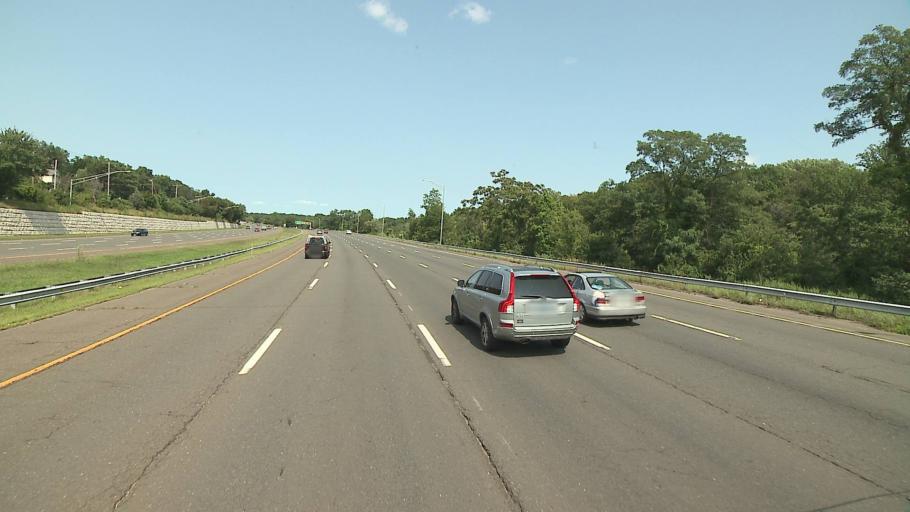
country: US
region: Connecticut
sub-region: Fairfield County
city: Trumbull
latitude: 41.2123
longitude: -73.1846
